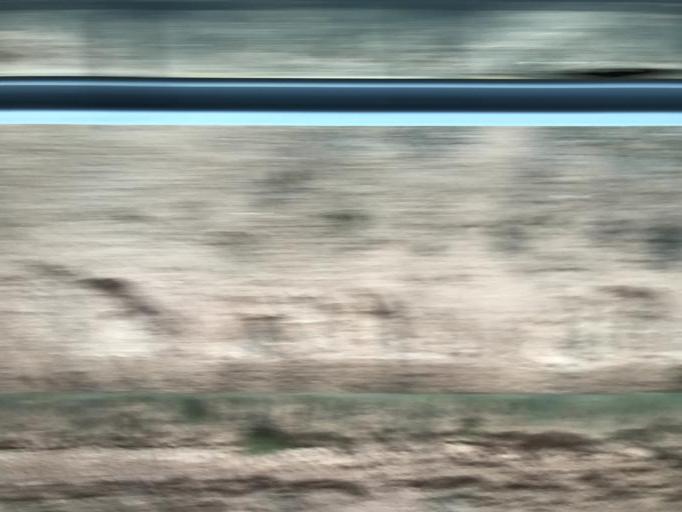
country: ES
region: Castille and Leon
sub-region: Provincia de Burgos
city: Lerma
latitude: 42.0103
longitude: -3.7534
